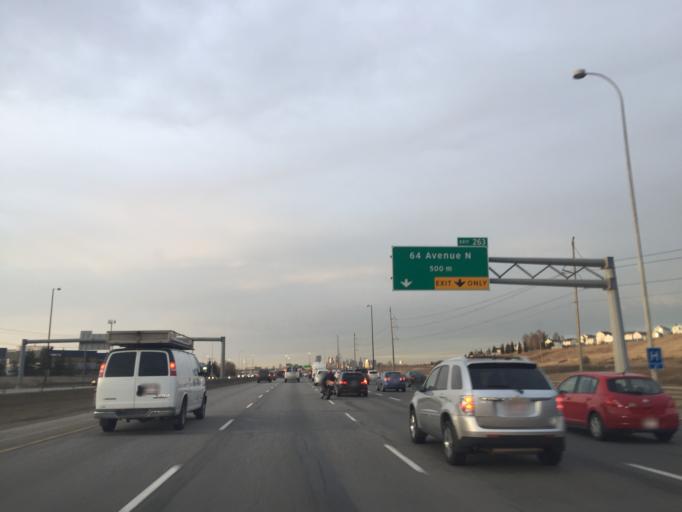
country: CA
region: Alberta
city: Calgary
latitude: 51.1205
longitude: -114.0464
